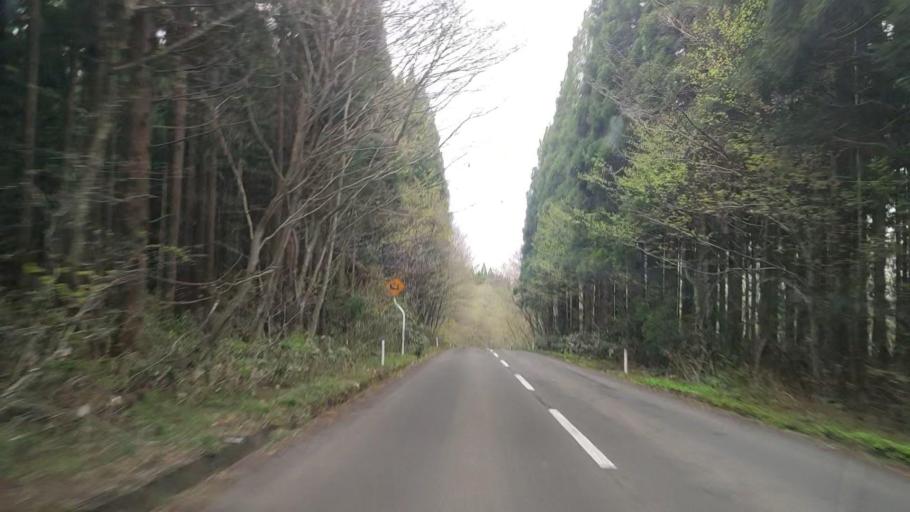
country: JP
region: Akita
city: Hanawa
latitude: 40.3857
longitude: 140.7927
